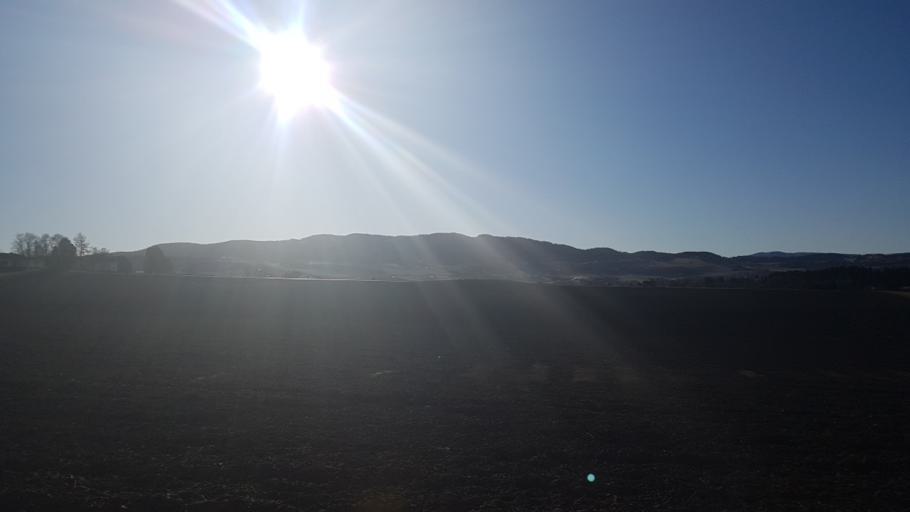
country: NO
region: Nord-Trondelag
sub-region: Levanger
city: Skogn
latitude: 63.6976
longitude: 11.1834
